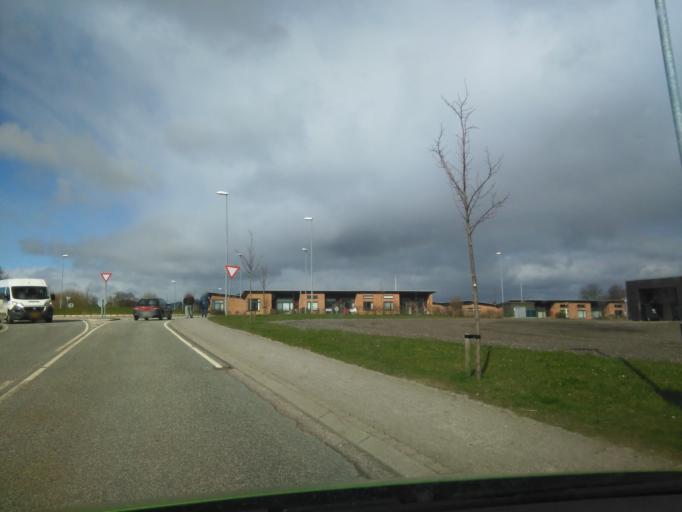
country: DK
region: Central Jutland
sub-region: Arhus Kommune
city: Marslet
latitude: 56.0611
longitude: 10.1563
